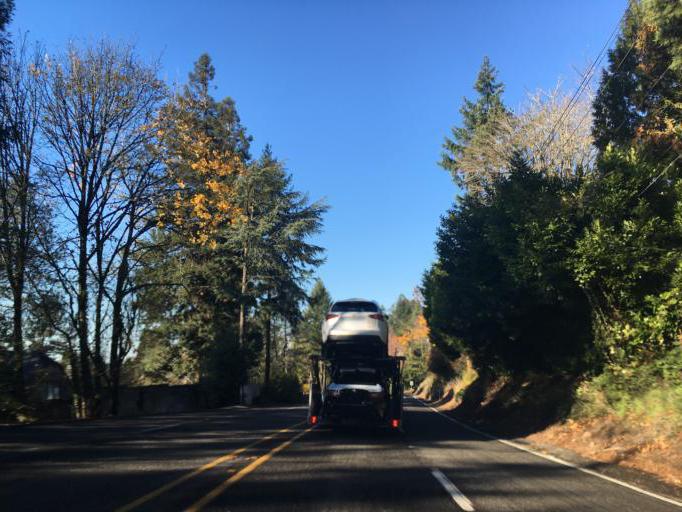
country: US
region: Oregon
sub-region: Washington County
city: West Slope
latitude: 45.4976
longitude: -122.7587
